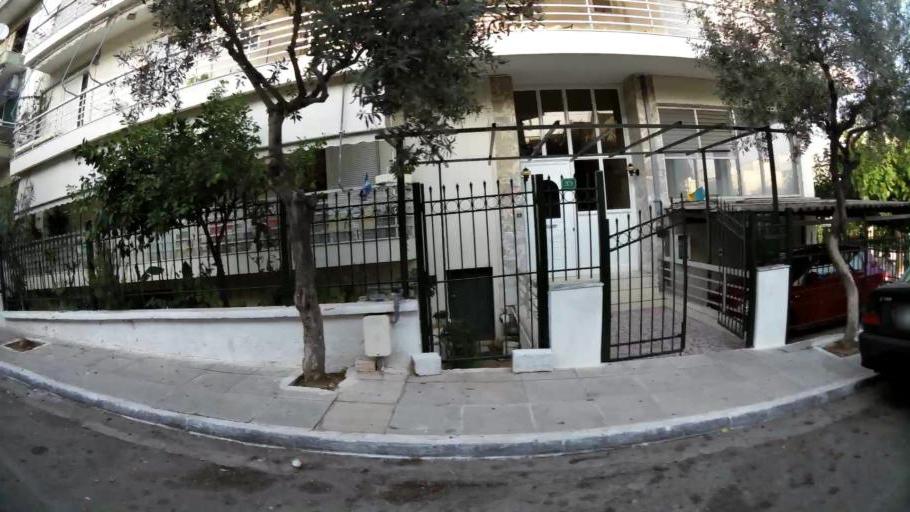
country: GR
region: Attica
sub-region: Nomarchia Athinas
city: Petroupolis
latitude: 38.0365
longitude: 23.6745
